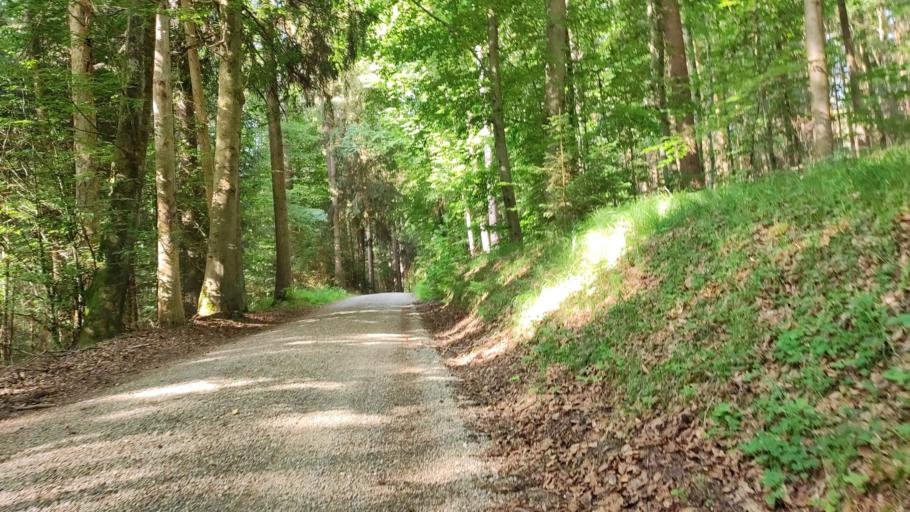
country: DE
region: Bavaria
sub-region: Swabia
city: Altenmunster
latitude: 48.4784
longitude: 10.5645
